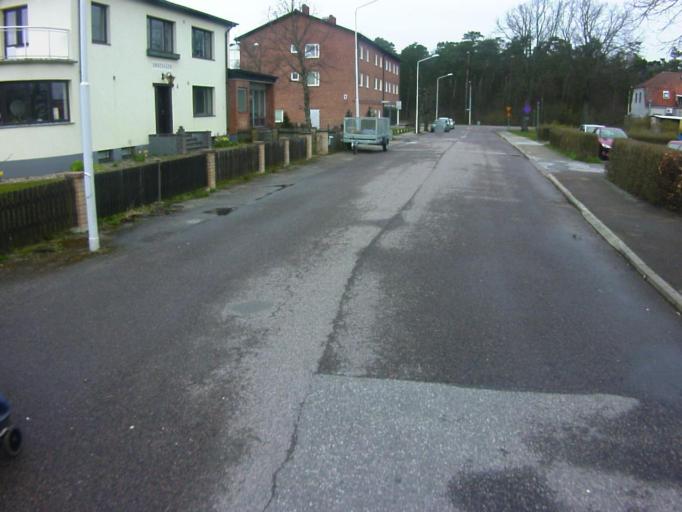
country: SE
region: Skane
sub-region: Kavlinge Kommun
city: Kaevlinge
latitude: 55.7749
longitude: 13.0957
